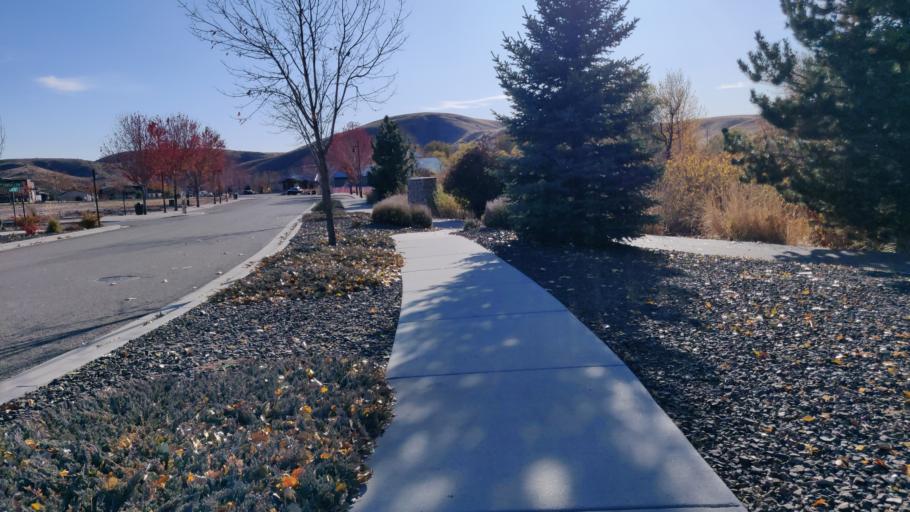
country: US
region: Idaho
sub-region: Ada County
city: Eagle
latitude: 43.7749
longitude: -116.2630
